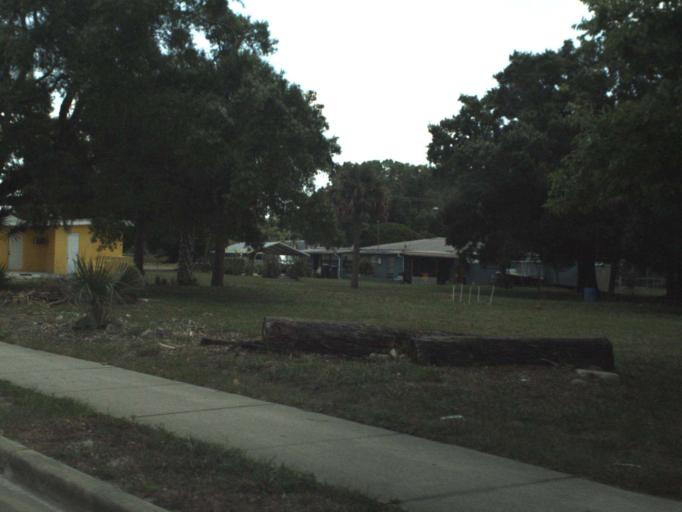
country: US
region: Florida
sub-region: Brevard County
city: Titusville
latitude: 28.6079
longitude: -80.8153
